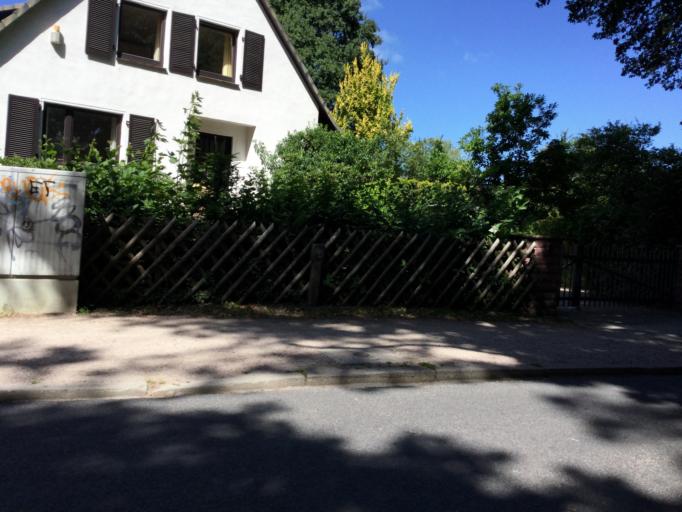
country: DE
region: Hamburg
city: Bergstedt
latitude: 53.6429
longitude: 10.1493
